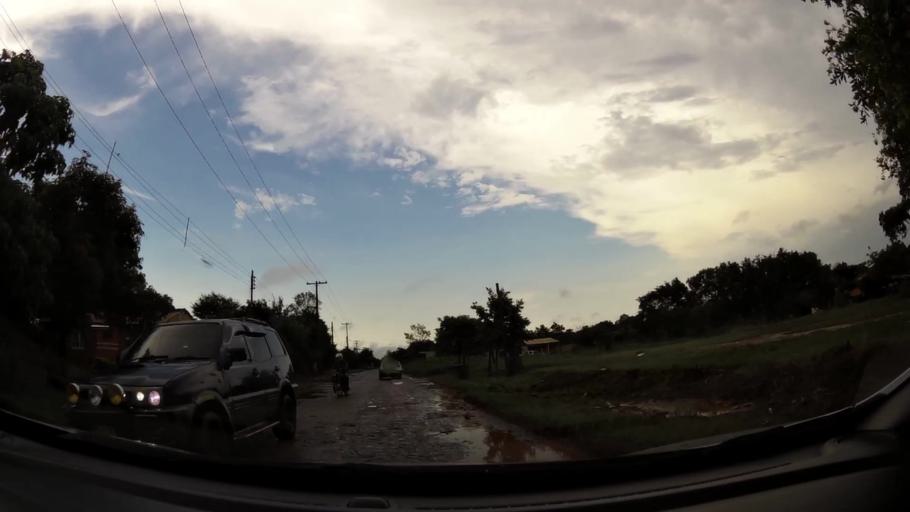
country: PY
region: Alto Parana
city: Presidente Franco
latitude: -25.5356
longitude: -54.6585
